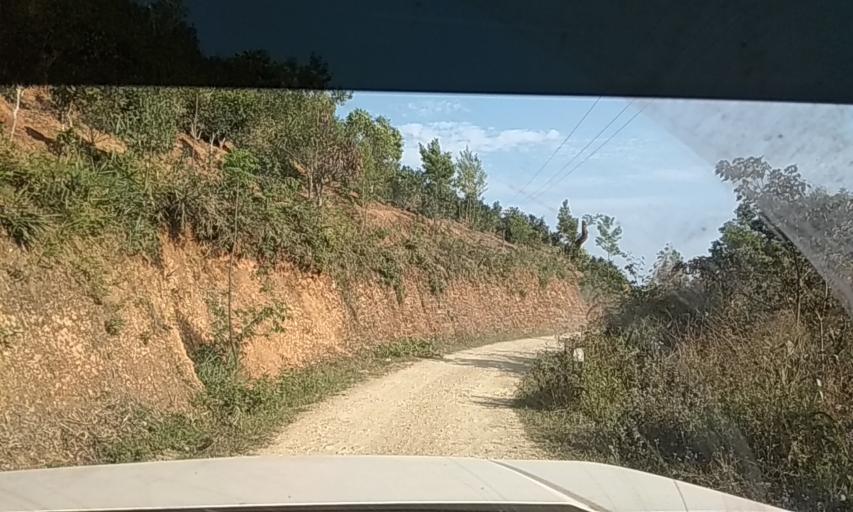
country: LA
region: Phongsali
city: Phongsali
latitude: 21.6584
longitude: 102.1633
